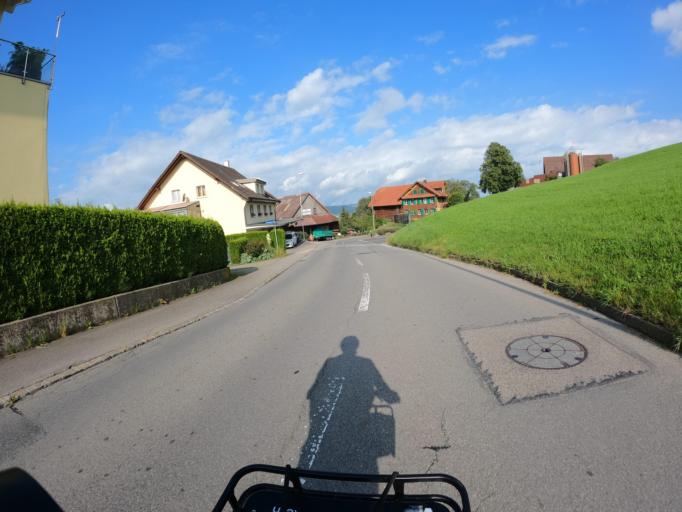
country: CH
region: Lucerne
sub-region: Hochdorf District
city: Hitzkirch
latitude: 47.2205
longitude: 8.2842
